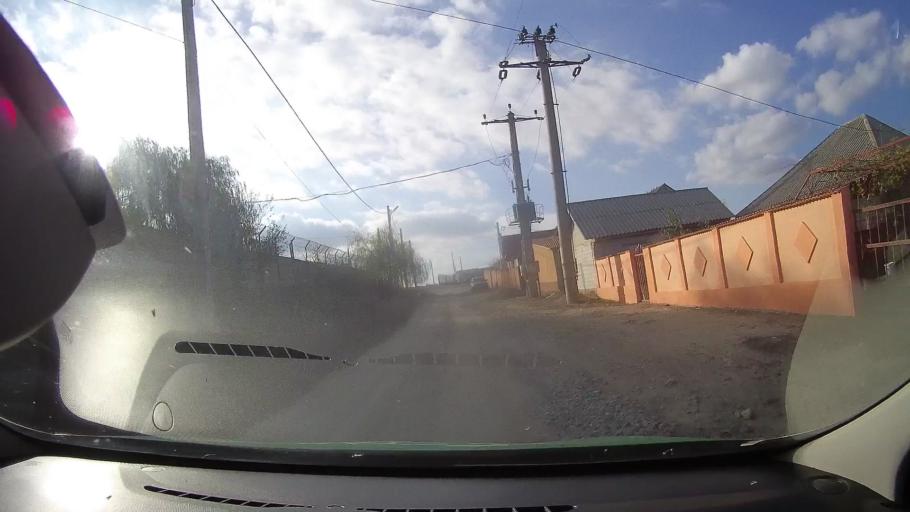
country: RO
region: Constanta
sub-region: Comuna Sacele
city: Sacele
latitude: 44.4807
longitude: 28.6488
